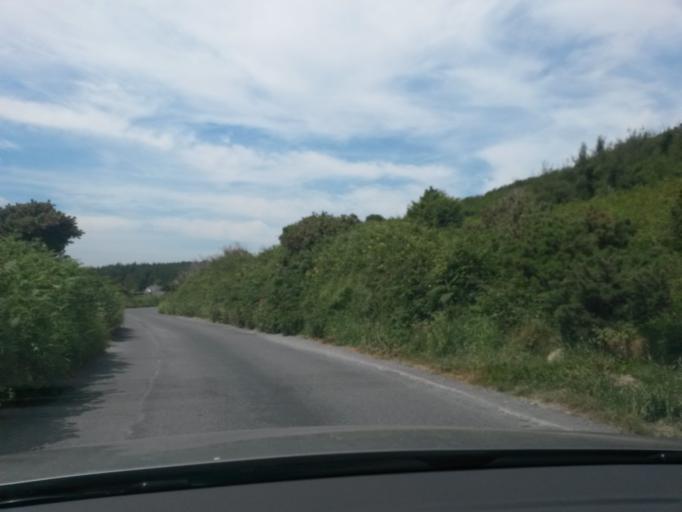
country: IE
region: Leinster
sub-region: Wicklow
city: Enniskerry
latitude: 53.1874
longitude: -6.2204
